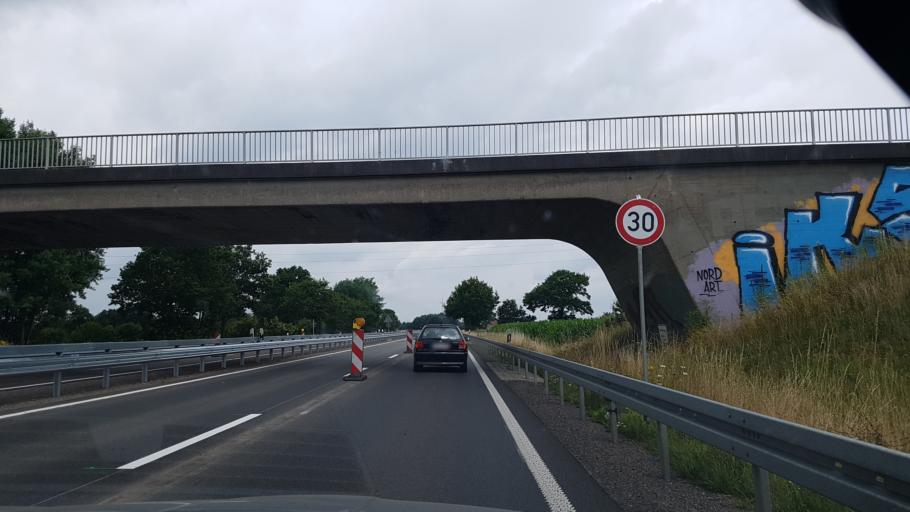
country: DE
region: Schleswig-Holstein
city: Neumunster
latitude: 54.1103
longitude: 9.9683
